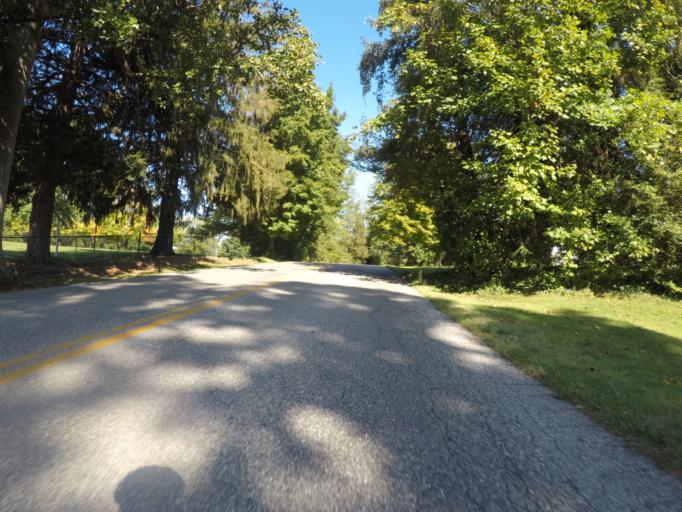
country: US
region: Kentucky
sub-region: Boyd County
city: Westwood
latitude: 38.4921
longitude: -82.6937
